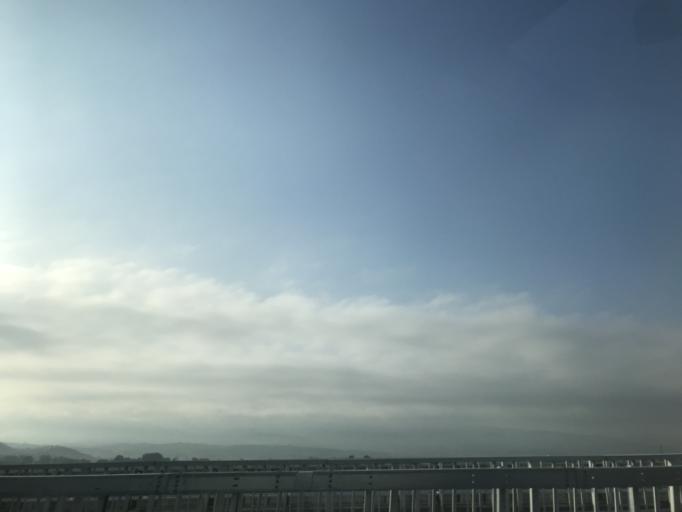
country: TR
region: Balikesir
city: Gobel
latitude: 39.9772
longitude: 28.1709
